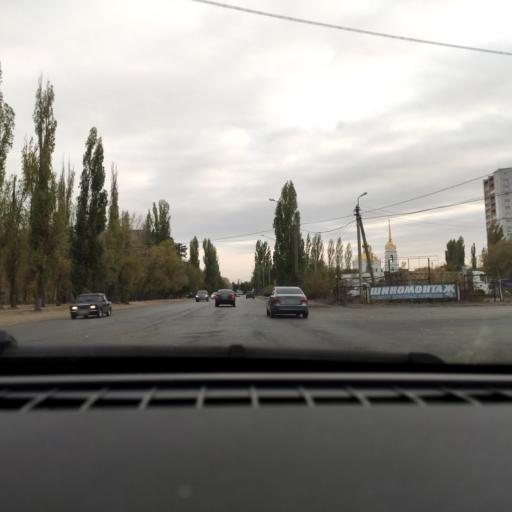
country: RU
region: Voronezj
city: Voronezh
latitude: 51.6374
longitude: 39.2641
